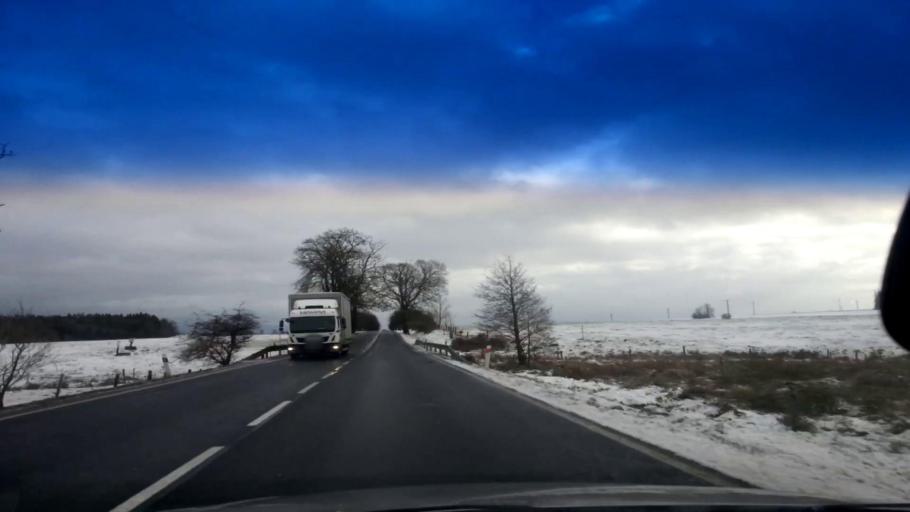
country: CZ
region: Karlovarsky
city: Hazlov
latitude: 50.1527
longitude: 12.2842
